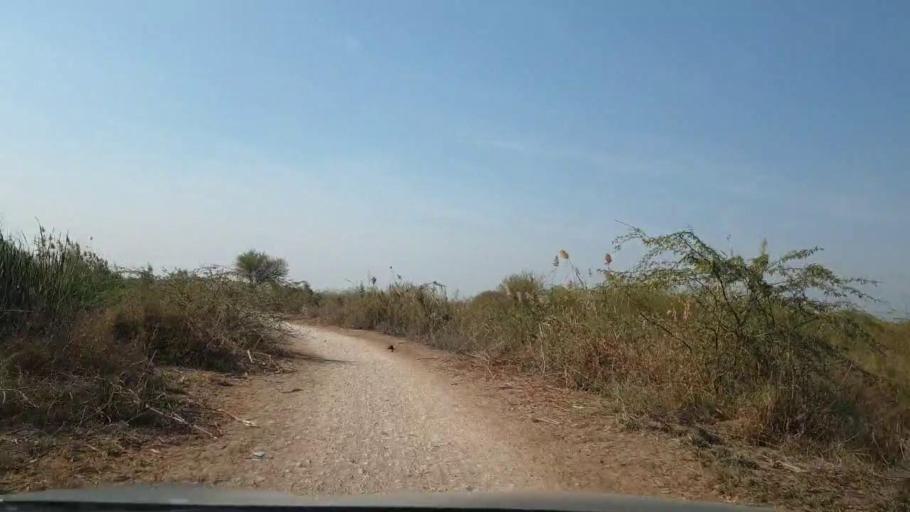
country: PK
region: Sindh
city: Berani
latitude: 25.7176
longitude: 68.7720
